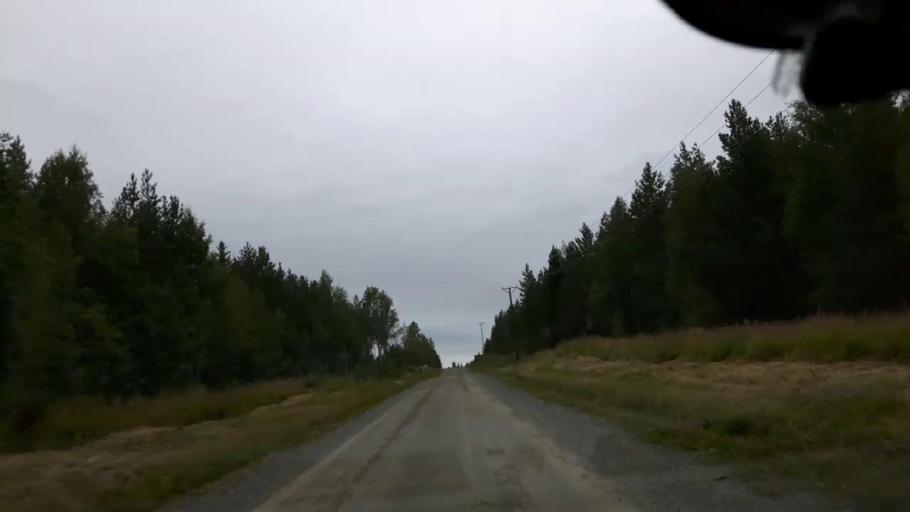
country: SE
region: Vaesternorrland
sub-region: Ange Kommun
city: Fransta
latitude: 62.8056
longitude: 16.0204
